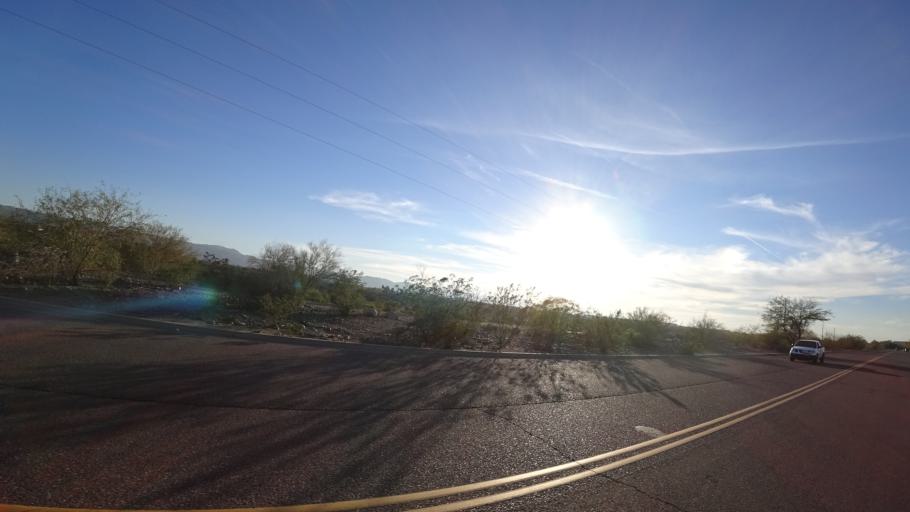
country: US
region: Arizona
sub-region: Maricopa County
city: Phoenix
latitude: 33.4202
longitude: -112.0492
